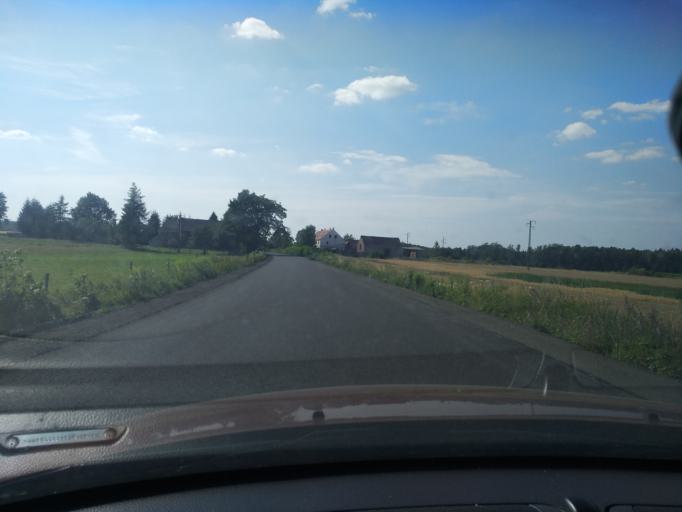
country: PL
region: Lower Silesian Voivodeship
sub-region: Powiat lubanski
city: Lesna
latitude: 51.0413
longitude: 15.2123
